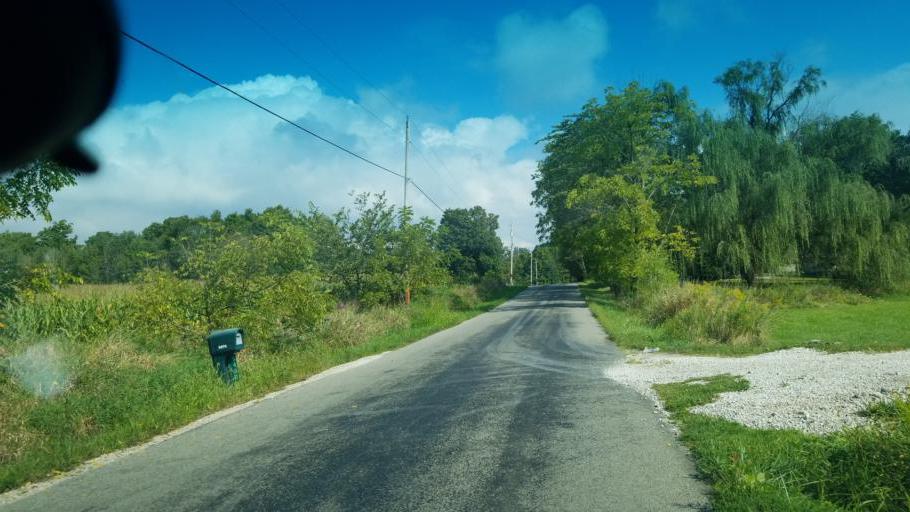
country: US
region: Ohio
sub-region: Licking County
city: Granville
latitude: 40.1753
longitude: -82.5629
